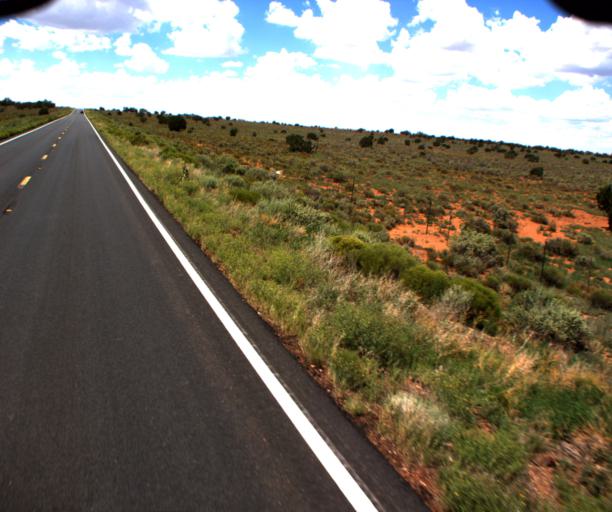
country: US
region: Arizona
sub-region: Coconino County
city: Williams
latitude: 35.6166
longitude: -112.0866
